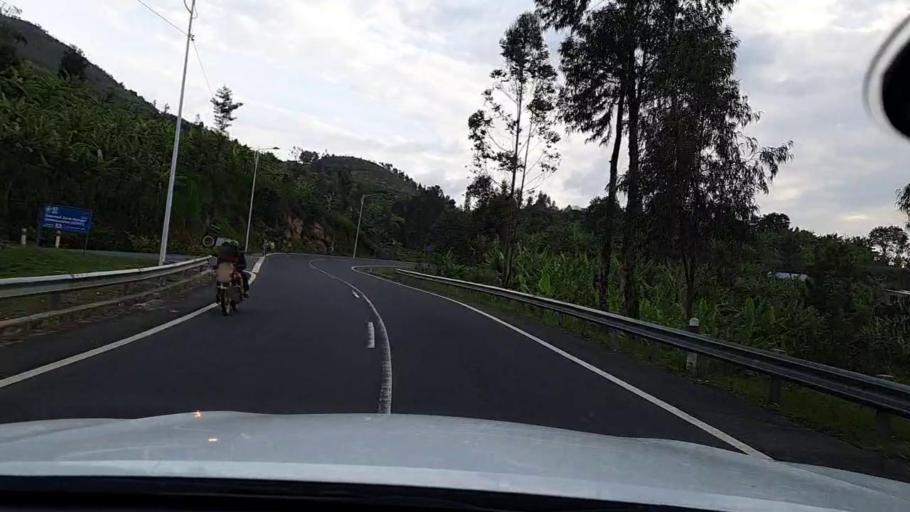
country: RW
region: Western Province
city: Kibuye
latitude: -2.0849
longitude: 29.4152
